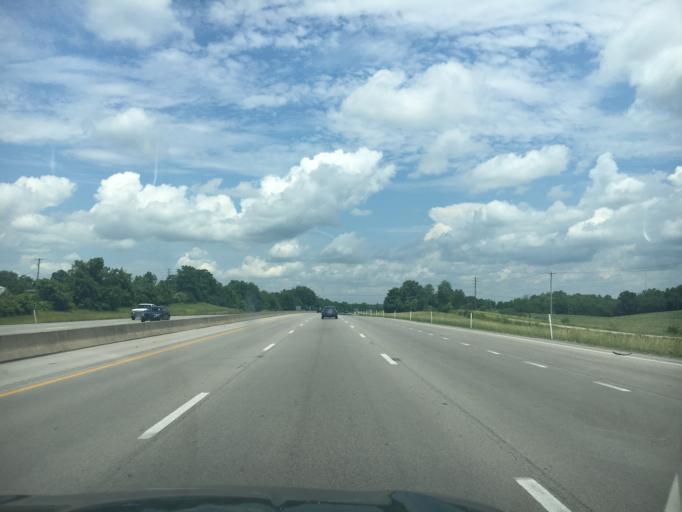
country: US
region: Kentucky
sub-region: Madison County
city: Richmond
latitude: 37.8469
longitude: -84.3290
